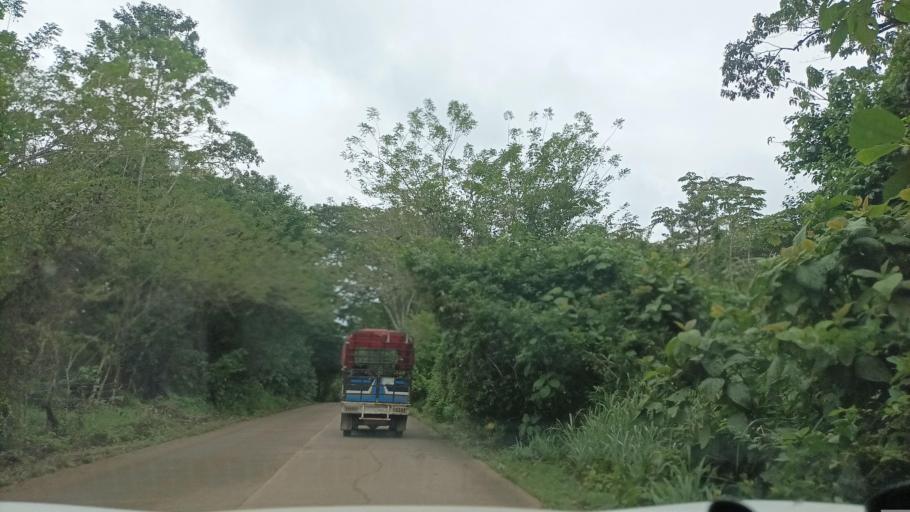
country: MX
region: Veracruz
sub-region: Uxpanapa
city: Poblado 10
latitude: 17.2792
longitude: -94.4864
